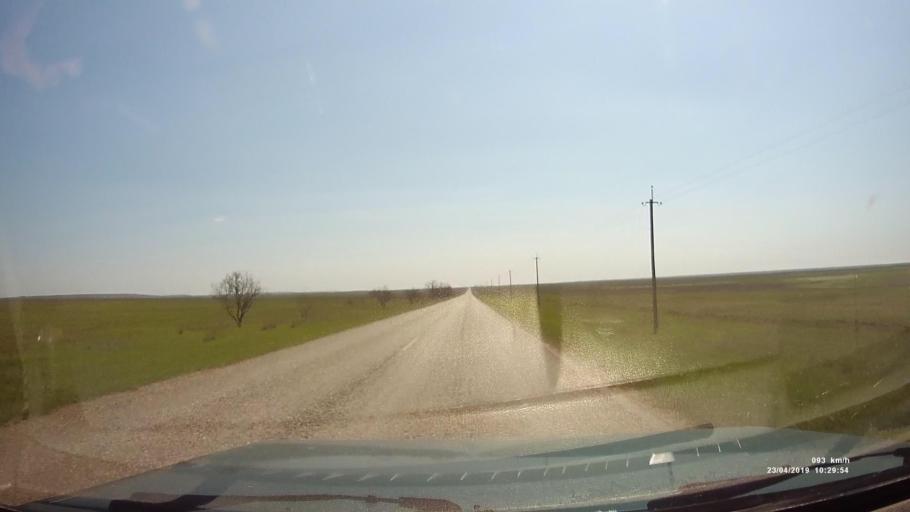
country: RU
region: Kalmykiya
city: Yashalta
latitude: 46.5955
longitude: 42.5346
